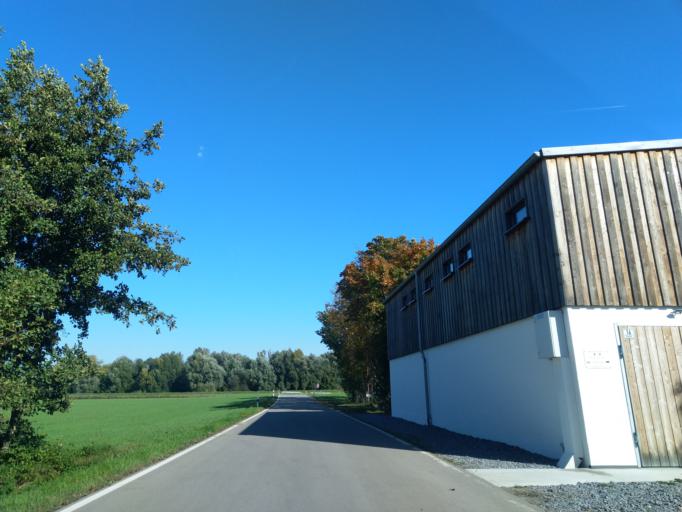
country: DE
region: Bavaria
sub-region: Lower Bavaria
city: Stephansposching
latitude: 48.8205
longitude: 12.8046
